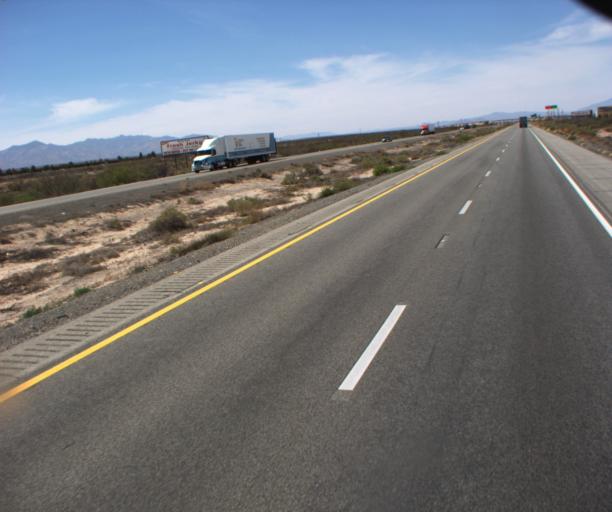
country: US
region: New Mexico
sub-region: Hidalgo County
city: Lordsburg
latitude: 32.2668
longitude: -109.2383
